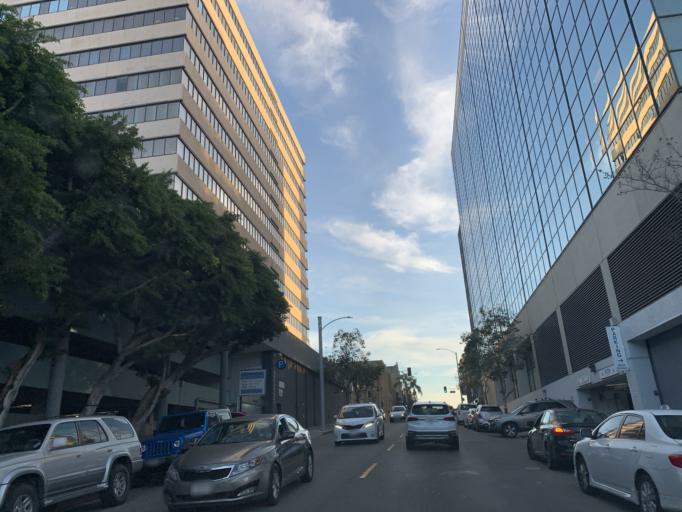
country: US
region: California
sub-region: Los Angeles County
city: Silver Lake
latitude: 34.0627
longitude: -118.2954
